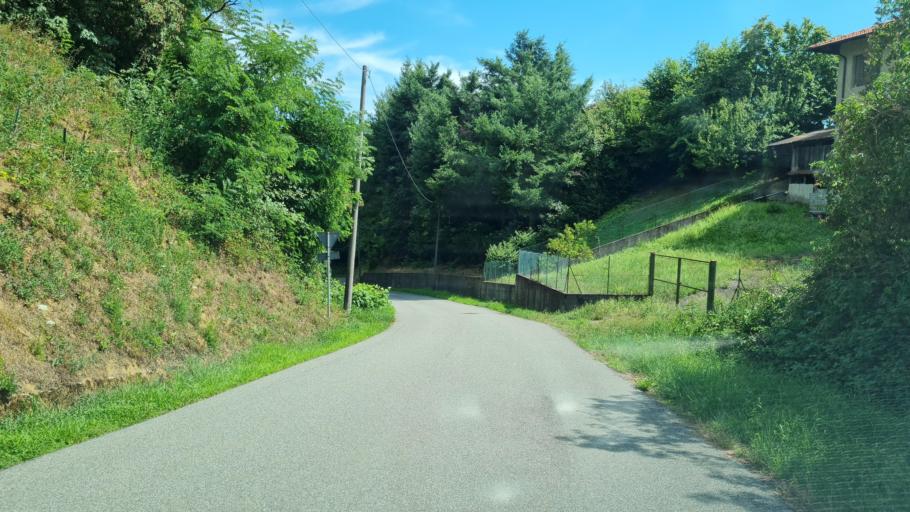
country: IT
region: Piedmont
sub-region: Provincia di Biella
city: Lessona
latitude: 45.5769
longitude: 8.2033
